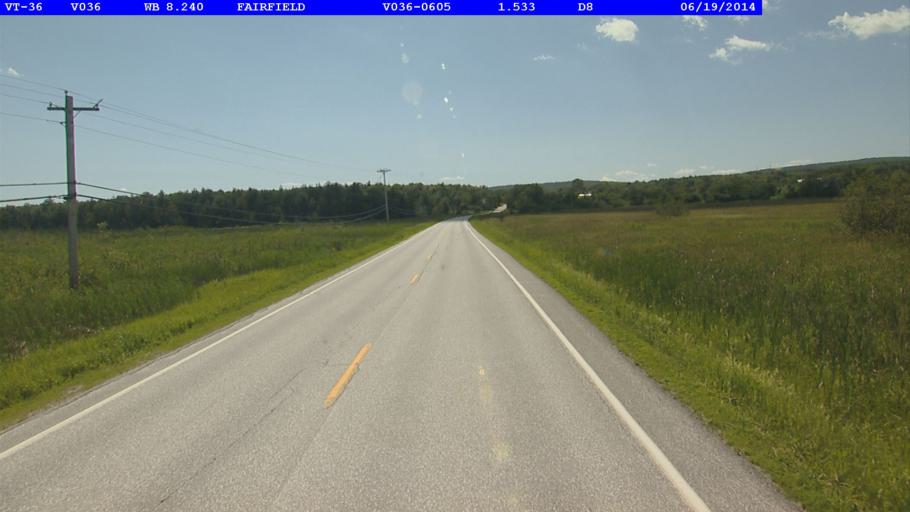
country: US
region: Vermont
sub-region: Franklin County
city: Saint Albans
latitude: 44.7874
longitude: -73.0011
